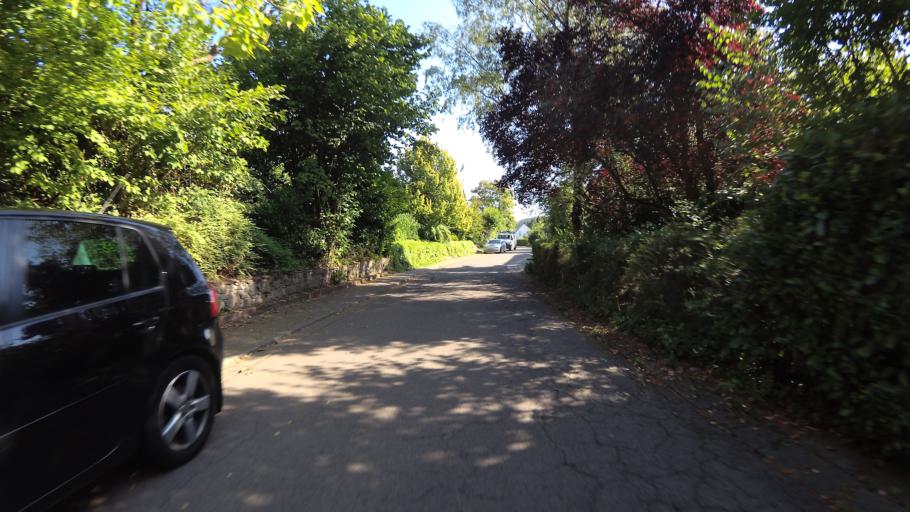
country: DE
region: Saarland
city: Illingen
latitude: 49.4101
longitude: 7.0184
